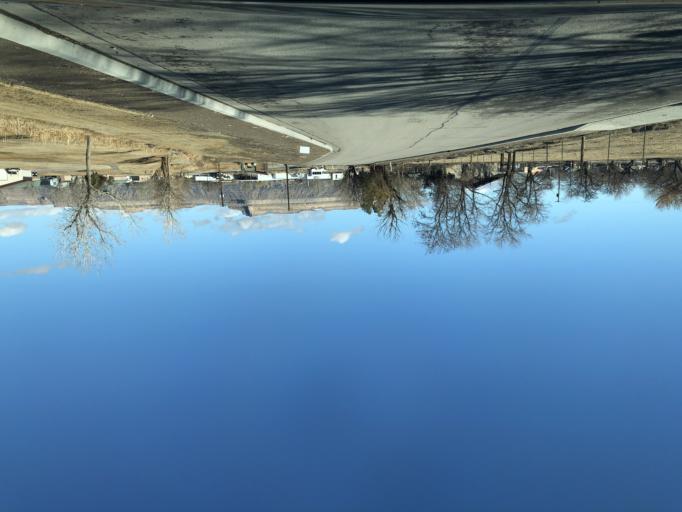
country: US
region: Utah
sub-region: Carbon County
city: East Carbon City
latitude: 38.9921
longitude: -110.1561
